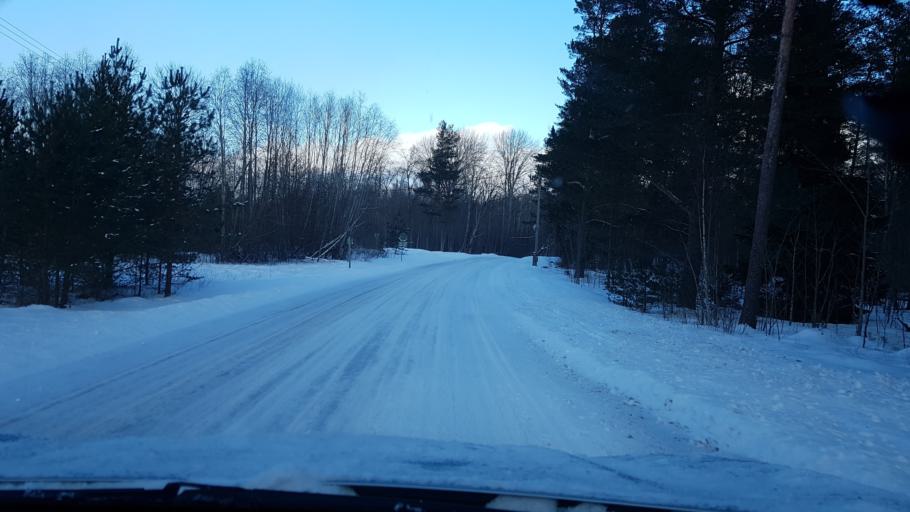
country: EE
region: Harju
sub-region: Nissi vald
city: Turba
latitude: 59.2205
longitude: 24.1408
